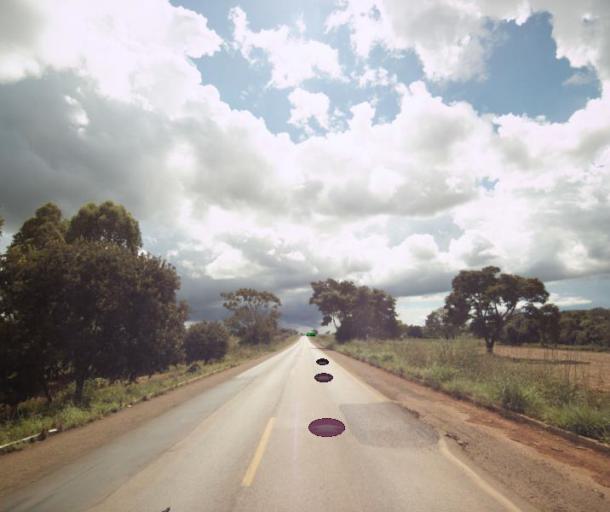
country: BR
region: Goias
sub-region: Uruacu
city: Uruacu
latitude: -14.7059
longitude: -49.1008
